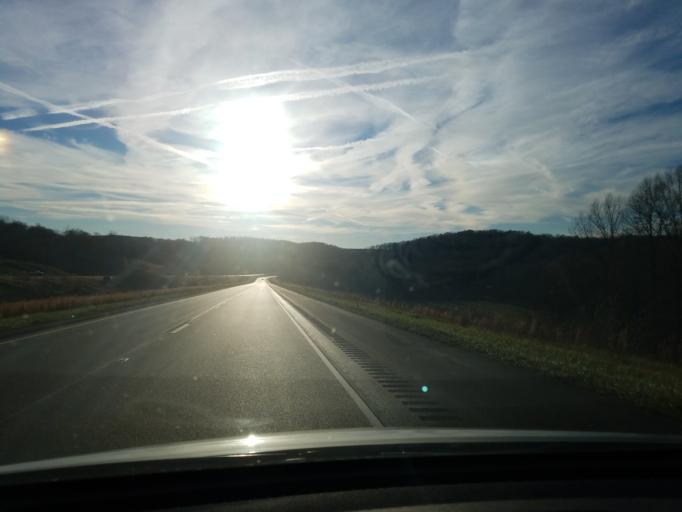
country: US
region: Indiana
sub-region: Crawford County
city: English
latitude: 38.2314
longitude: -86.6294
